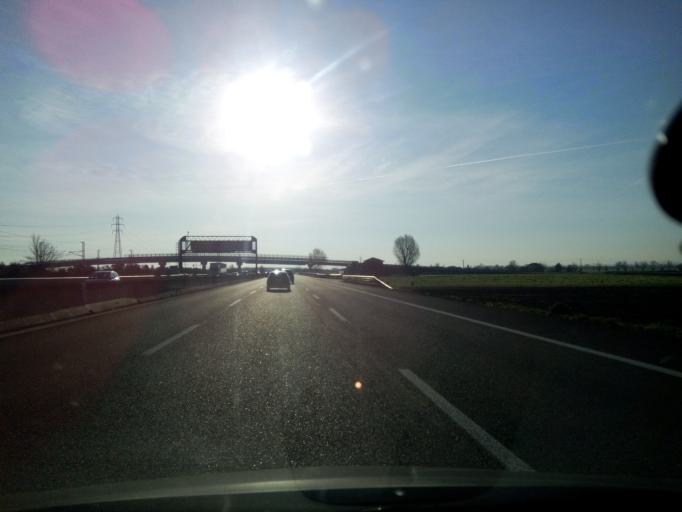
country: IT
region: Emilia-Romagna
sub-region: Provincia di Parma
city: Soragna
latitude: 44.8850
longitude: 10.1175
